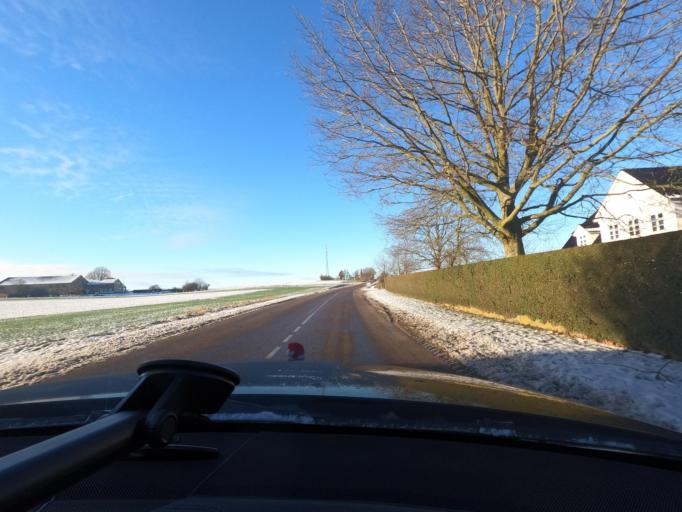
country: DK
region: South Denmark
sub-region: Sonderborg Kommune
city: Horuphav
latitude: 54.8735
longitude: 9.9317
